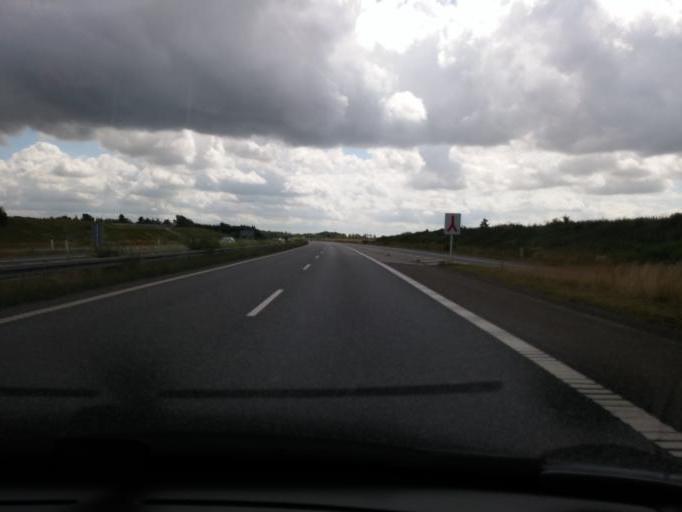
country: DK
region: South Denmark
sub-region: Faaborg-Midtfyn Kommune
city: Arslev
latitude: 55.3030
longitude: 10.4362
